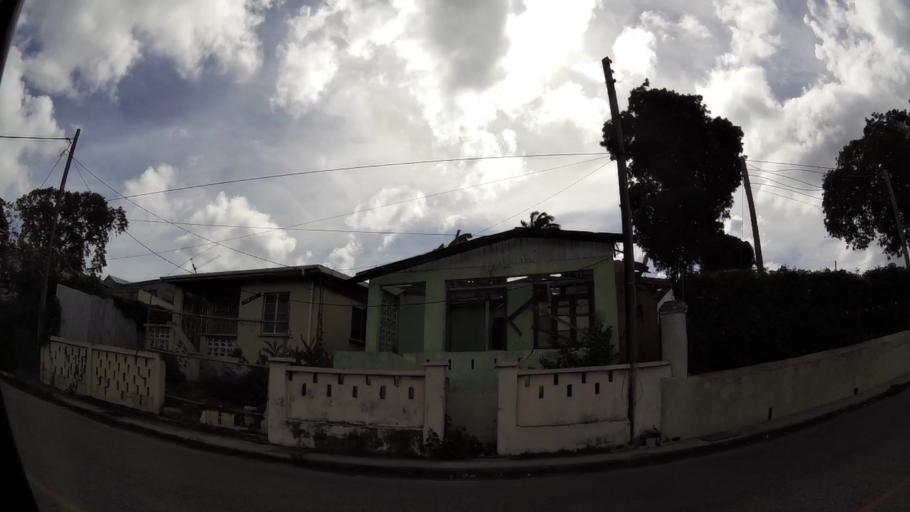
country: BB
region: Saint Michael
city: Bridgetown
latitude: 13.0959
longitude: -59.6089
